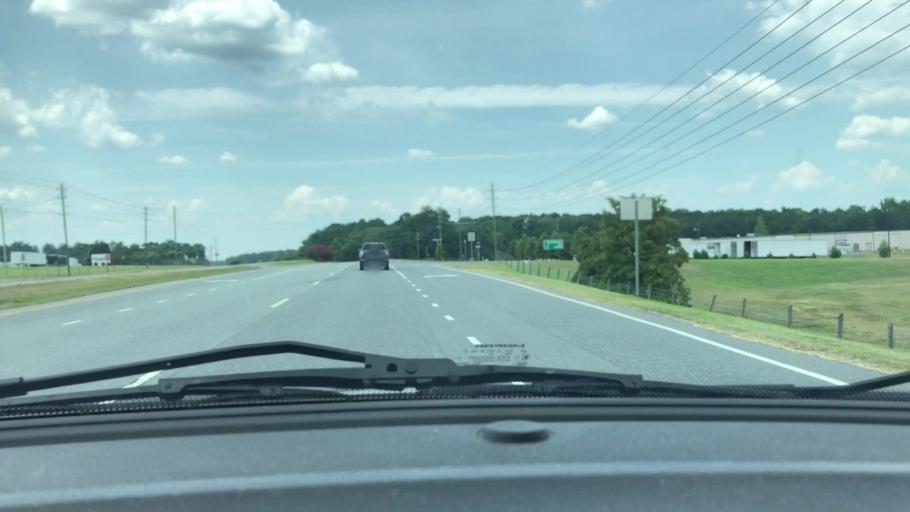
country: US
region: North Carolina
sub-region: Lee County
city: Sanford
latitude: 35.5149
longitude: -79.2152
